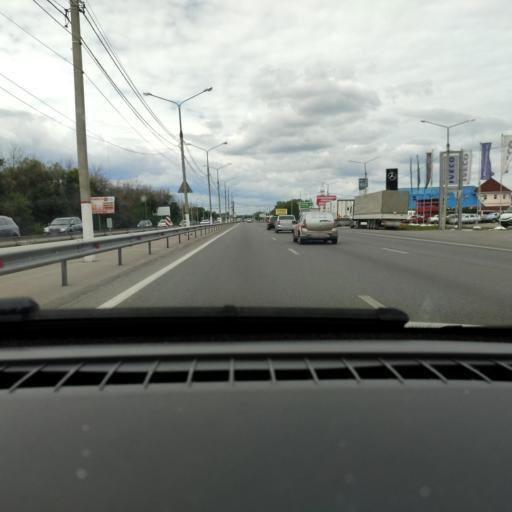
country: RU
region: Voronezj
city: Novaya Usman'
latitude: 51.6381
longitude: 39.3228
